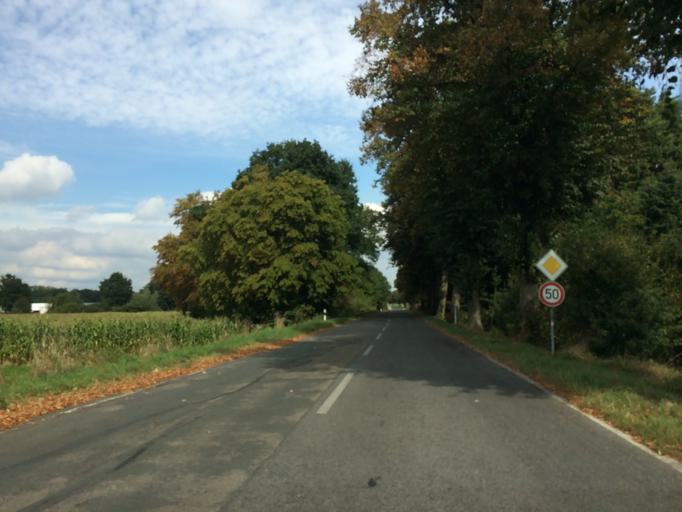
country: DE
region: North Rhine-Westphalia
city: Marl
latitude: 51.7037
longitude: 7.0917
